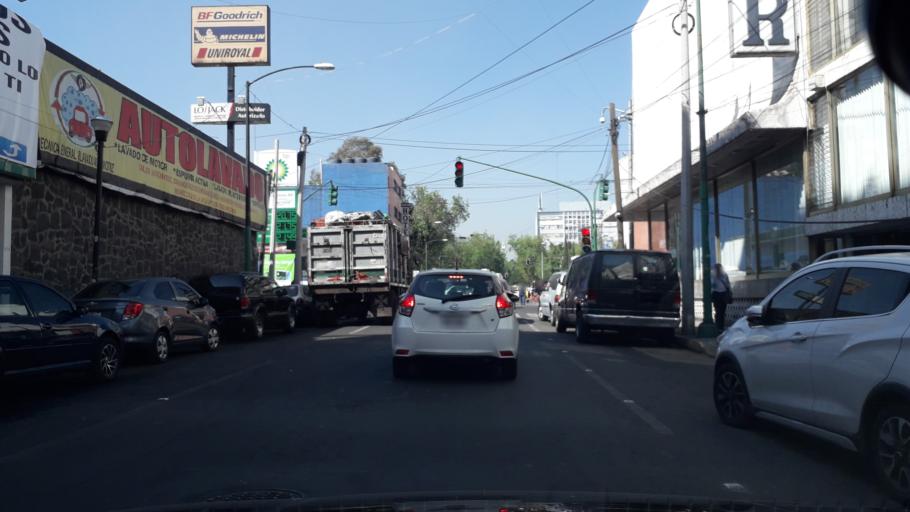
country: MX
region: Mexico City
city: Cuauhtemoc
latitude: 19.4405
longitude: -99.1512
